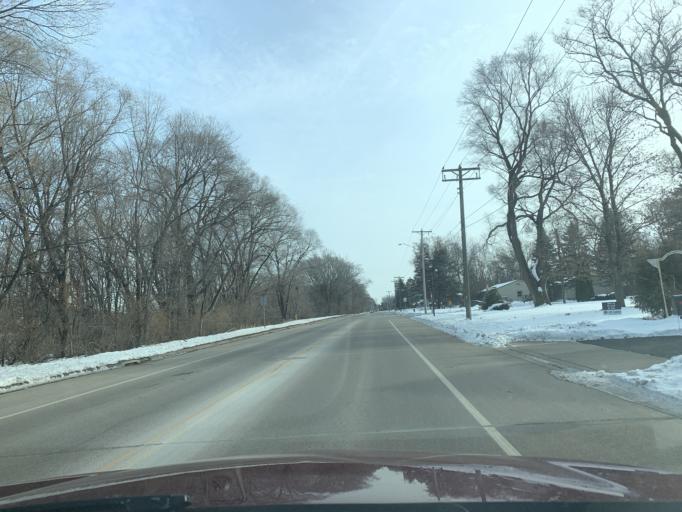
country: US
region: Minnesota
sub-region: Washington County
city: Saint Paul Park
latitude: 44.8372
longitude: -92.9736
